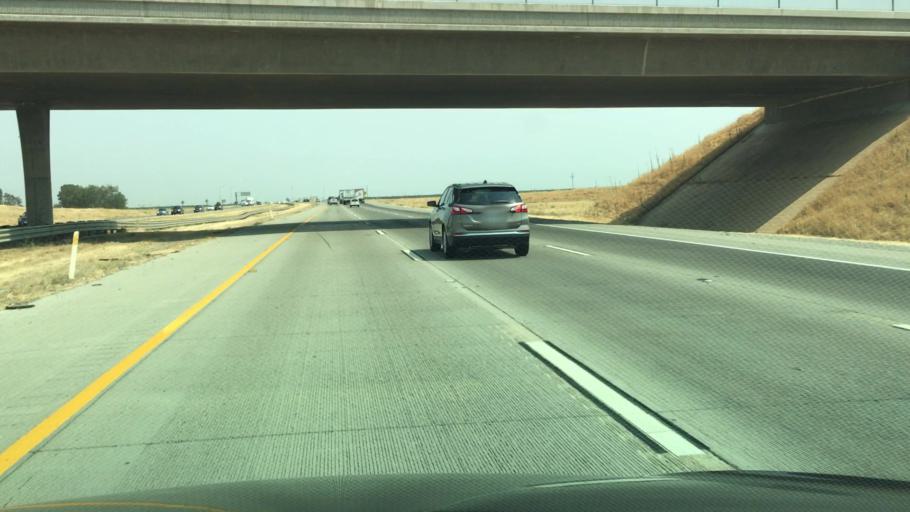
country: US
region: California
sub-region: Madera County
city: Fairmead
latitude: 37.0656
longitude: -120.1866
